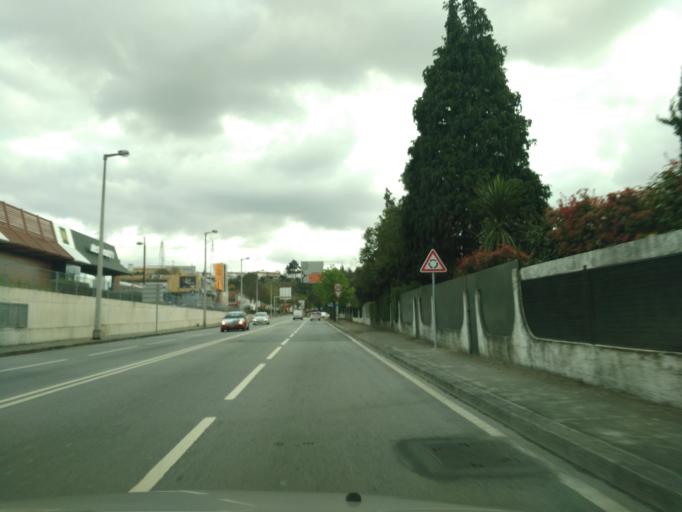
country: PT
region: Braga
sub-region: Guimaraes
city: Urgeses
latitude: 41.4323
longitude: -8.3019
